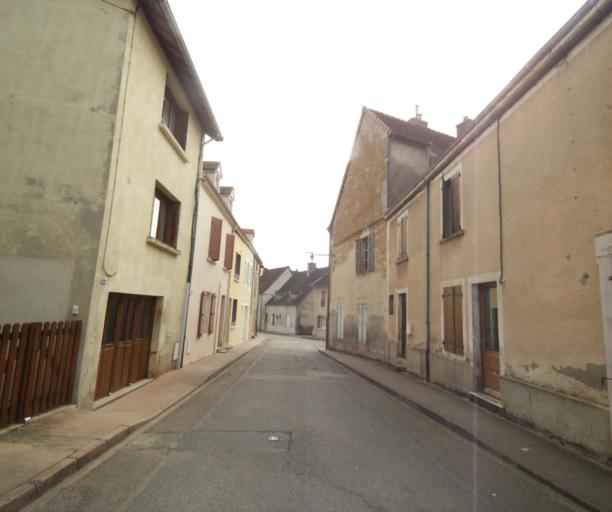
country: FR
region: Bourgogne
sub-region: Departement de Saone-et-Loire
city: Charolles
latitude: 46.4346
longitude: 4.2721
